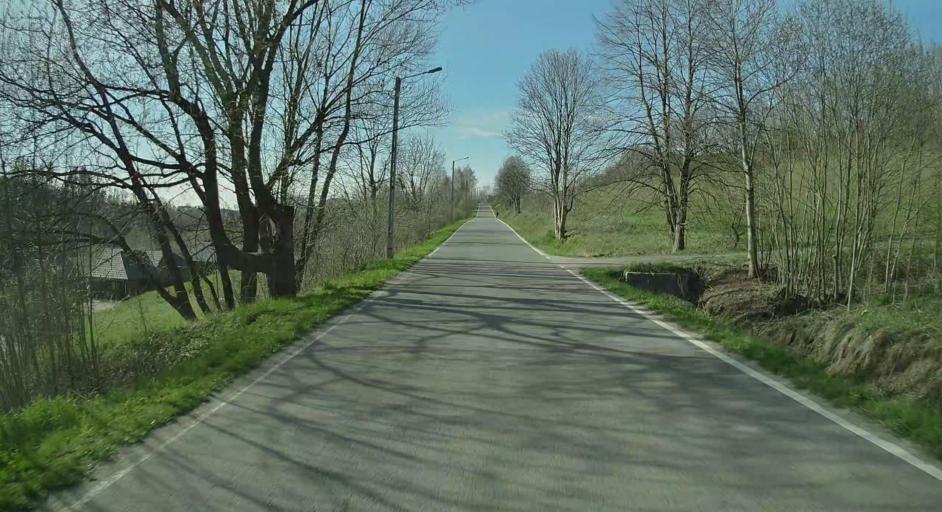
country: PL
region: Lower Silesian Voivodeship
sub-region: Powiat klodzki
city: Lewin Klodzki
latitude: 50.3992
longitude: 16.2962
